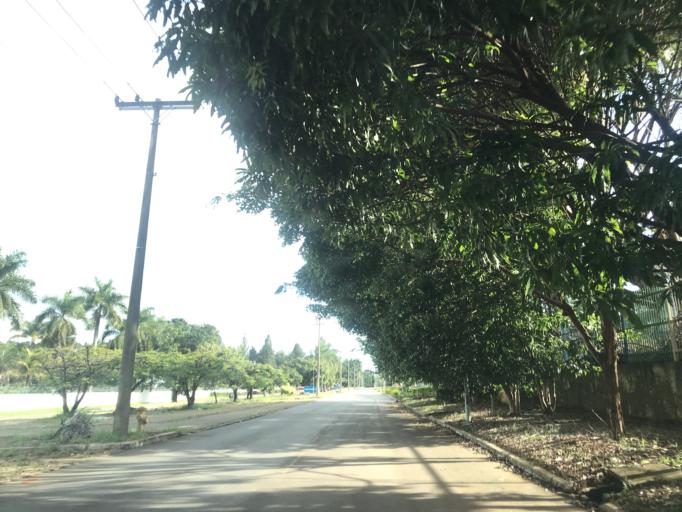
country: BR
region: Federal District
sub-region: Brasilia
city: Brasilia
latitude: -15.8148
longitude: -47.8858
